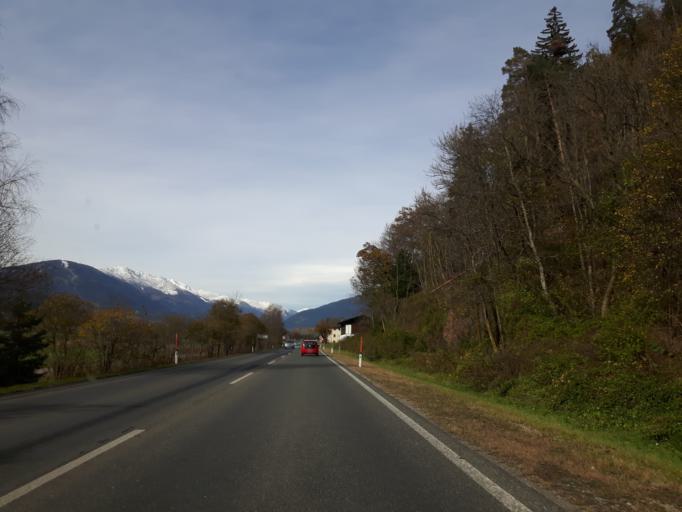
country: AT
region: Tyrol
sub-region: Politischer Bezirk Lienz
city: Lavant
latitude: 46.8069
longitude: 12.8594
